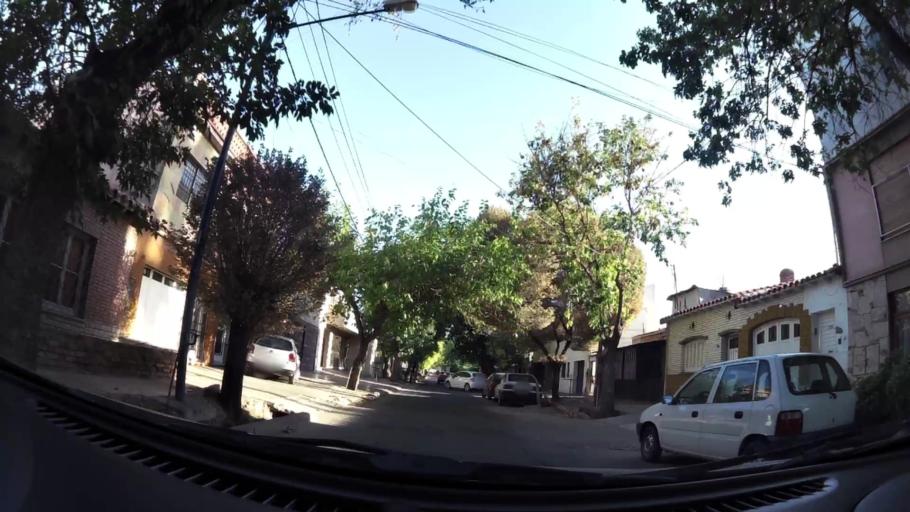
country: AR
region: Mendoza
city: Mendoza
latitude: -32.9050
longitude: -68.8412
